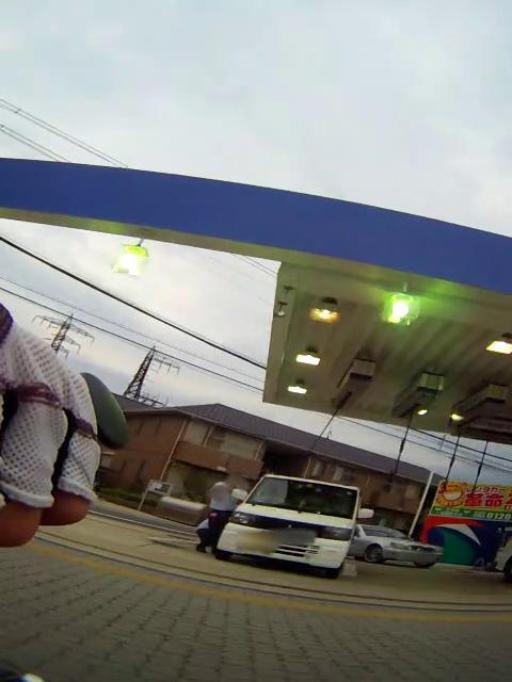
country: JP
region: Osaka
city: Moriguchi
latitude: 34.7260
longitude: 135.5756
